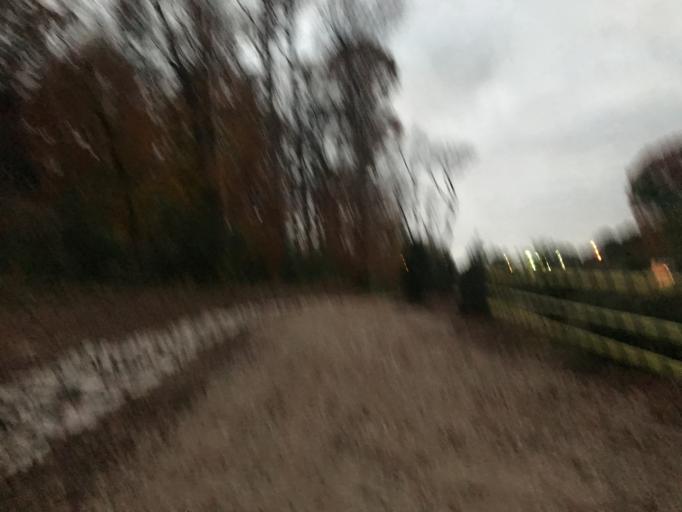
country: US
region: North Carolina
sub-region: Wake County
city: West Raleigh
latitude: 35.8362
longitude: -78.6636
